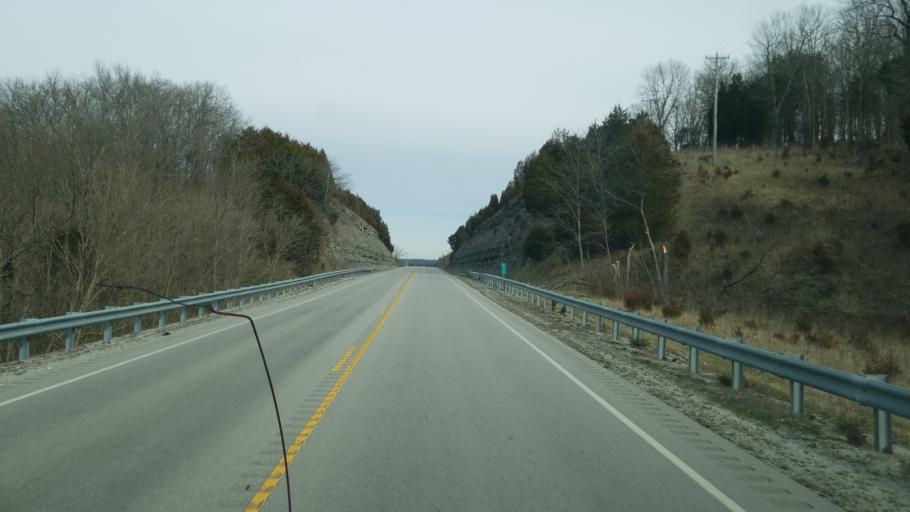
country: US
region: Kentucky
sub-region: Nicholas County
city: Carlisle
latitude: 38.4131
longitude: -84.0066
